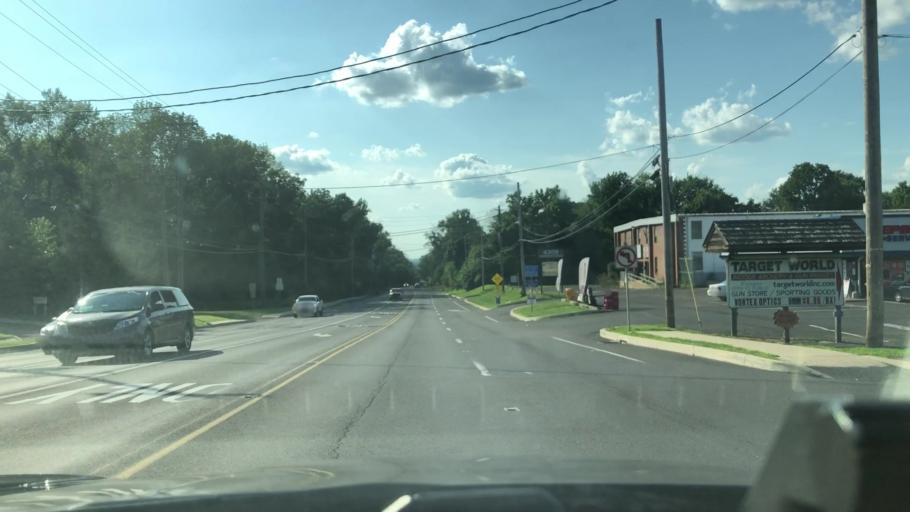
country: US
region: Pennsylvania
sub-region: Bucks County
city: Brittany Farms-Highlands
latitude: 40.2661
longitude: -75.2288
